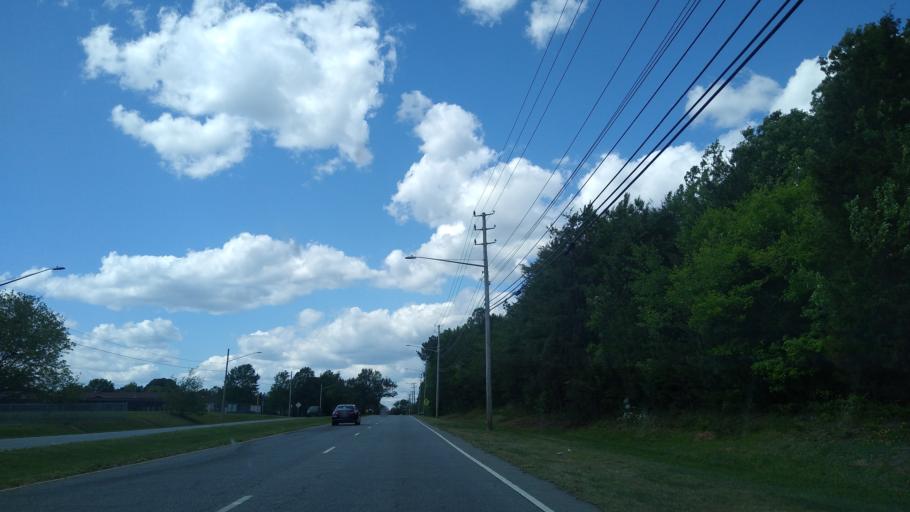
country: US
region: North Carolina
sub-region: Guilford County
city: High Point
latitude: 36.0005
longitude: -80.0095
